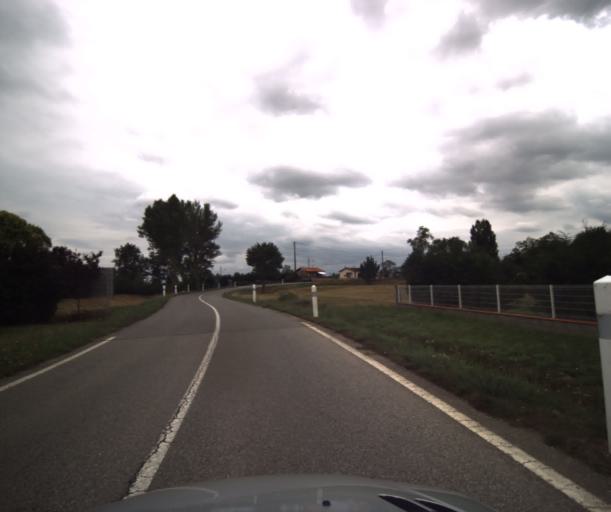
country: FR
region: Midi-Pyrenees
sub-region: Departement de la Haute-Garonne
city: Labarthe-sur-Leze
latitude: 43.4568
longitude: 1.4140
